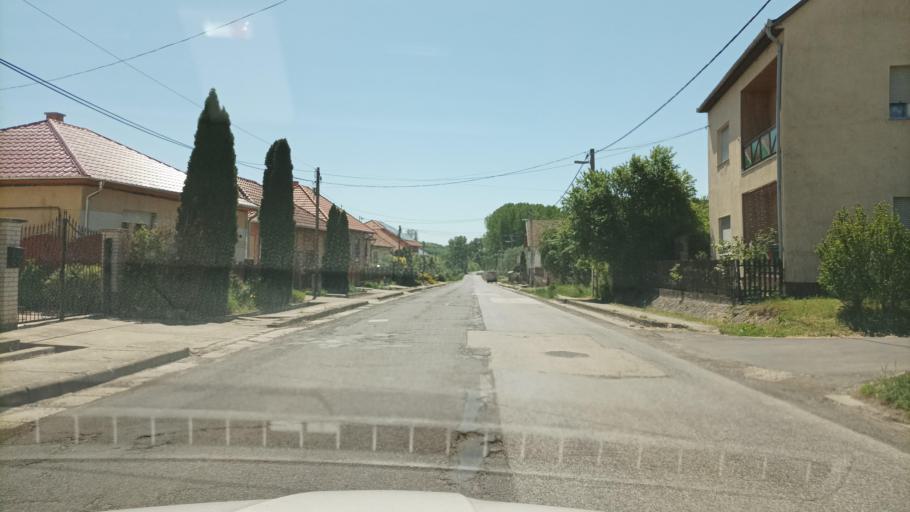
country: HU
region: Pest
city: Galgamacsa
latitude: 47.6993
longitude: 19.3984
